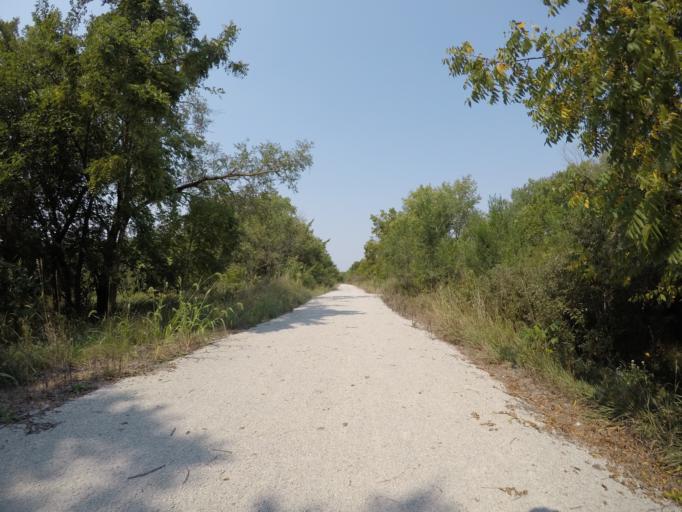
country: US
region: Nebraska
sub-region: Gage County
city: Beatrice
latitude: 40.2524
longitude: -96.6988
